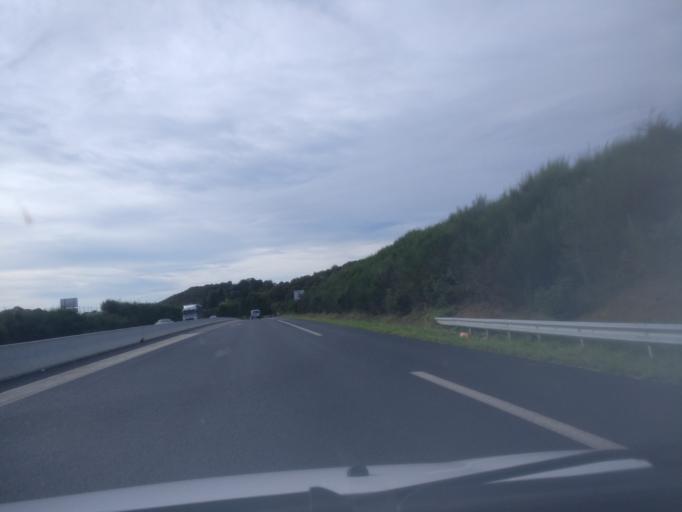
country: FR
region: Lower Normandy
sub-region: Departement de la Manche
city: Sartilly
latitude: 48.7474
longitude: -1.4422
